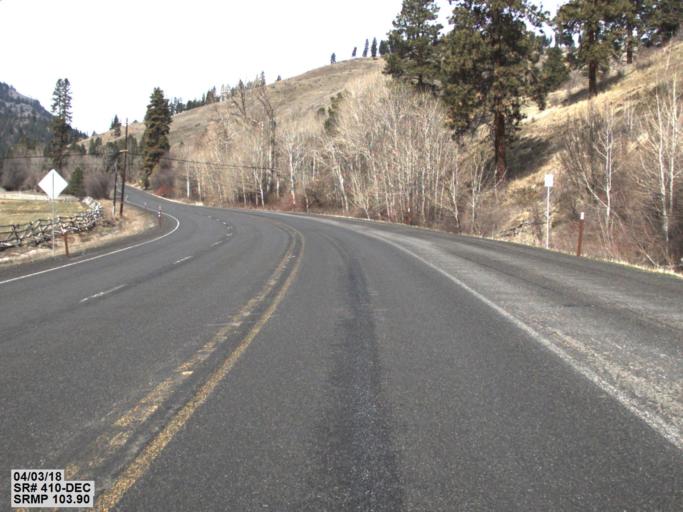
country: US
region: Washington
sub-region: Yakima County
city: Tieton
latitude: 46.8657
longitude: -120.9576
